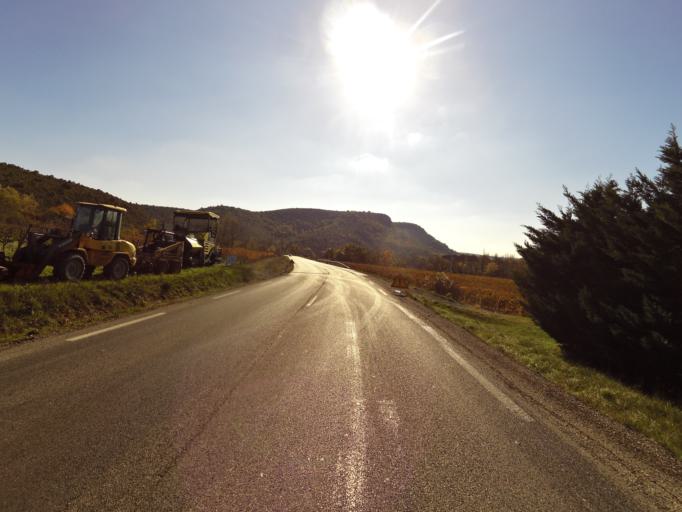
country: FR
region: Rhone-Alpes
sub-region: Departement de l'Ardeche
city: Largentiere
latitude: 44.5275
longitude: 4.3388
